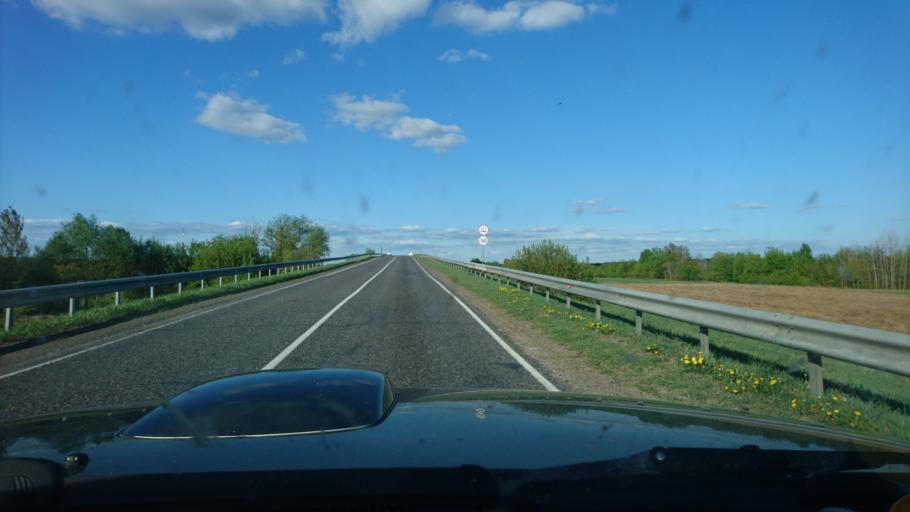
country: BY
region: Brest
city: Nyakhachava
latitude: 52.6373
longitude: 25.1921
